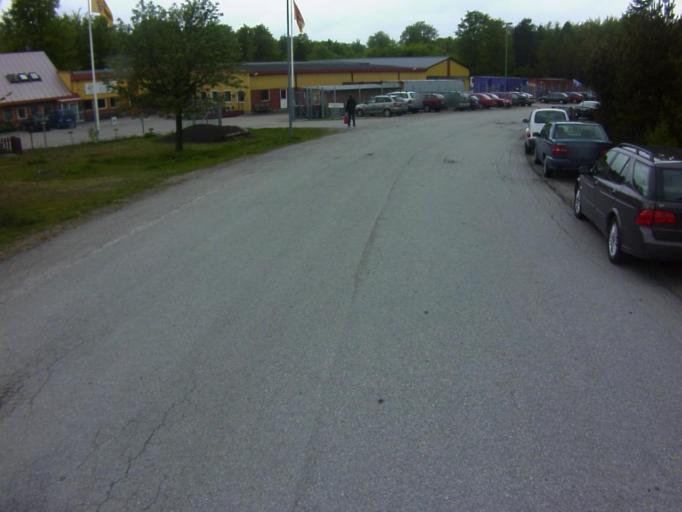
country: SE
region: Blekinge
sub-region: Solvesborgs Kommun
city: Soelvesborg
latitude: 56.0567
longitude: 14.5655
